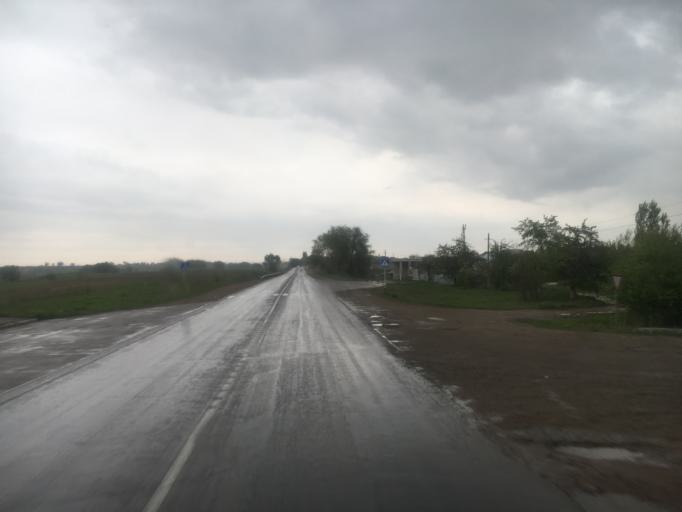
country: KZ
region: Almaty Oblysy
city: Burunday
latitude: 43.2905
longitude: 76.6733
